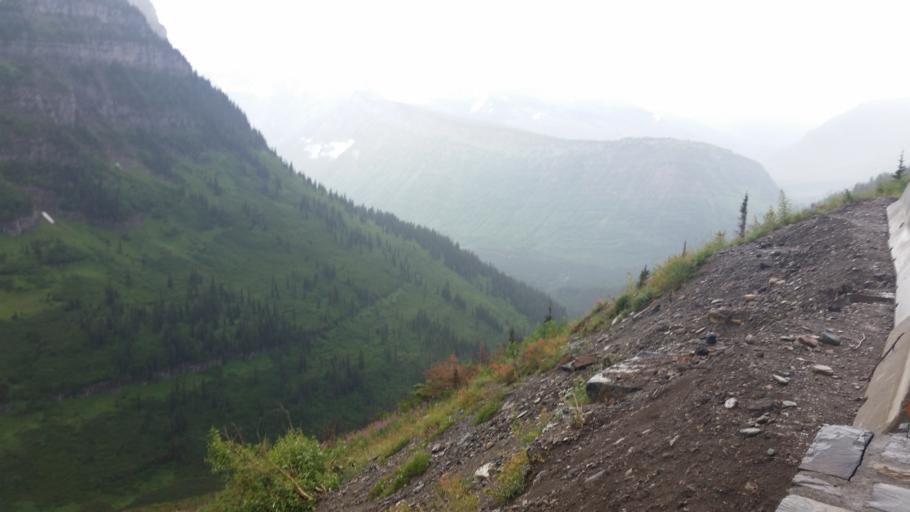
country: US
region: Montana
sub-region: Flathead County
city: Columbia Falls
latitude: 48.7138
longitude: -113.7182
